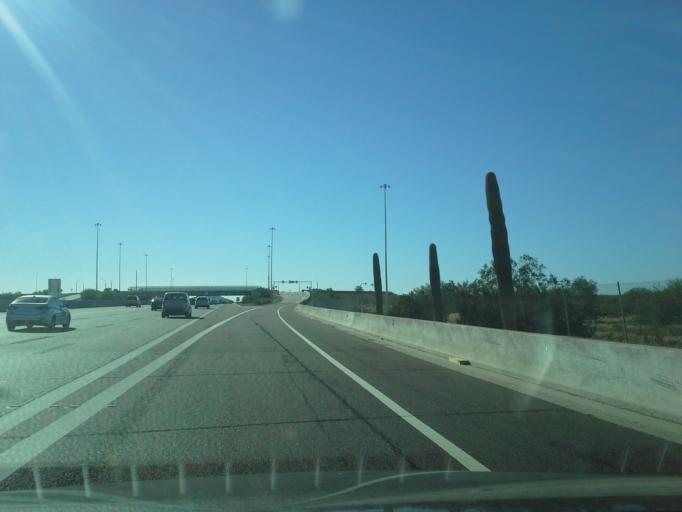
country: US
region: Arizona
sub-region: Maricopa County
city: Paradise Valley
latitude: 33.6609
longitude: -111.9376
